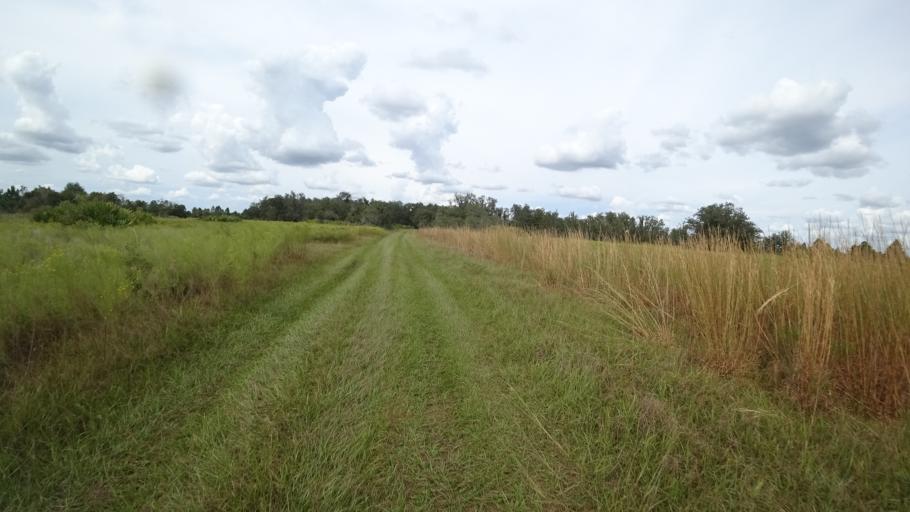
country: US
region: Florida
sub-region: Hillsborough County
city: Wimauma
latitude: 27.5504
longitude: -82.1358
